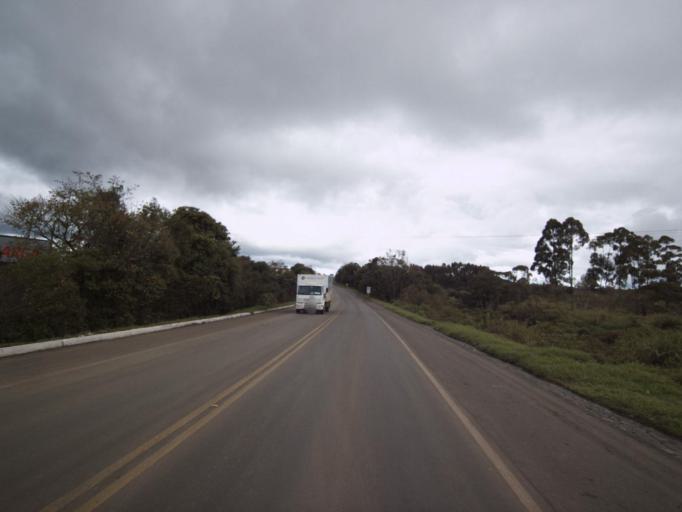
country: BR
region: Santa Catarina
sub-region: Concordia
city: Concordia
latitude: -27.2469
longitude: -51.9526
